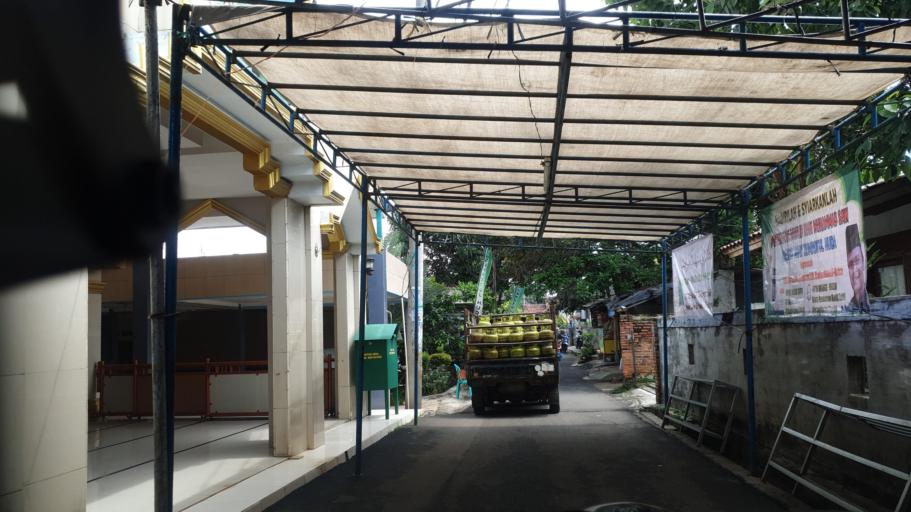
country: ID
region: West Java
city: Pamulang
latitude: -6.3378
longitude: 106.7698
